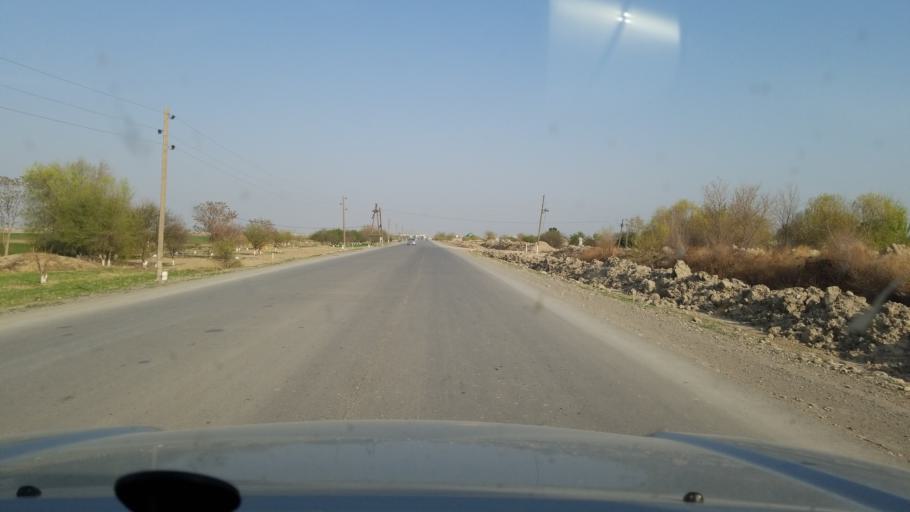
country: AF
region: Jowzjan
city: Qarqin
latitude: 37.5177
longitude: 65.9712
